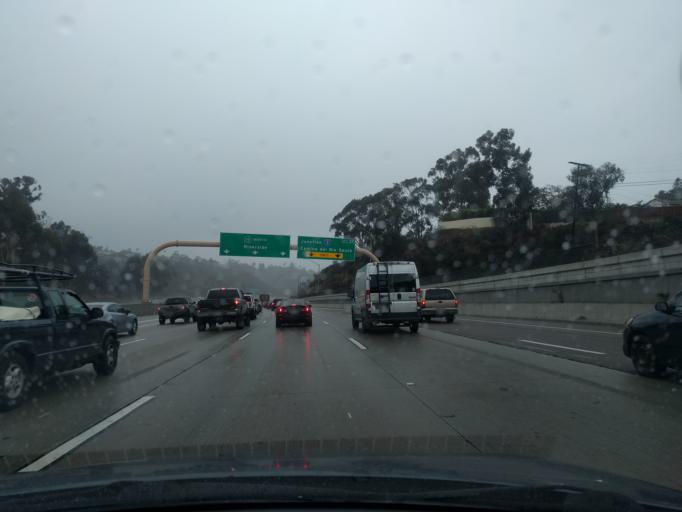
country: US
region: California
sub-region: San Diego County
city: San Diego
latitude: 32.7654
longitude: -117.1097
